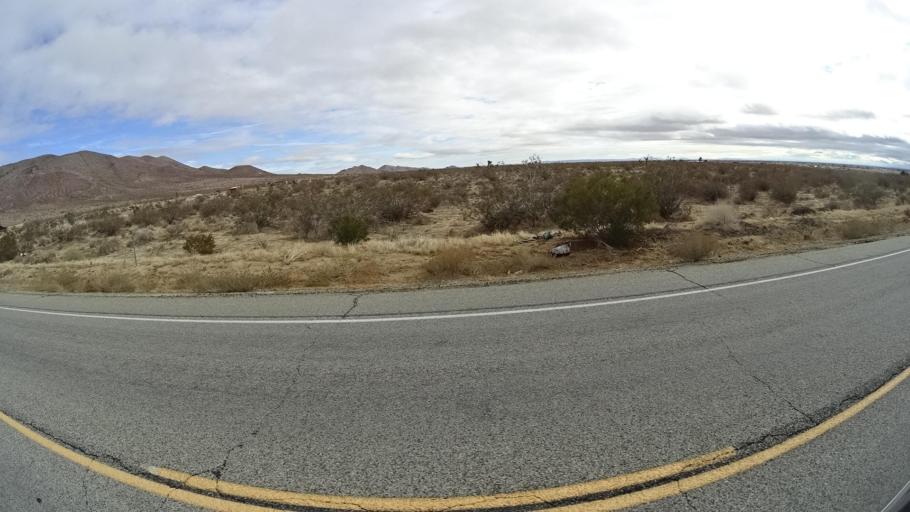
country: US
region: California
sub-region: Kern County
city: Rosamond
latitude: 34.8695
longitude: -118.2911
